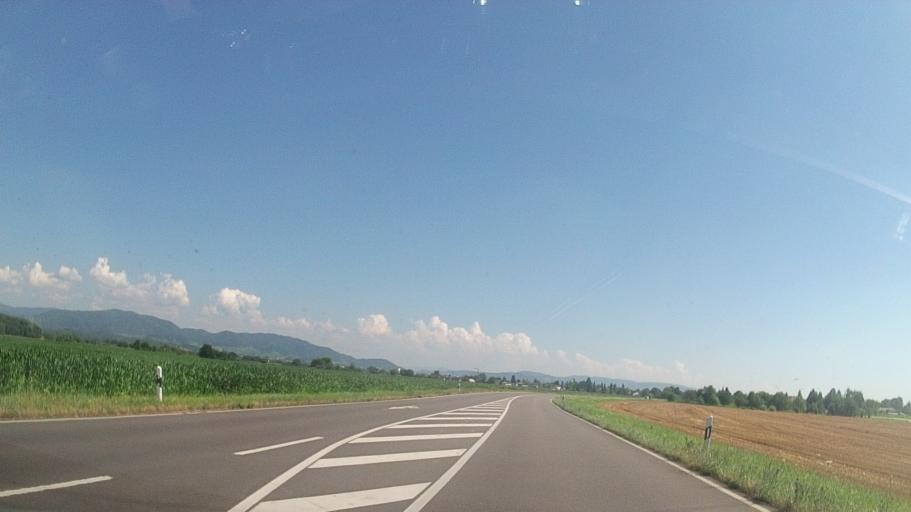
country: DE
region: Baden-Wuerttemberg
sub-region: Freiburg Region
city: Willstatt
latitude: 48.5186
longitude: 7.9253
